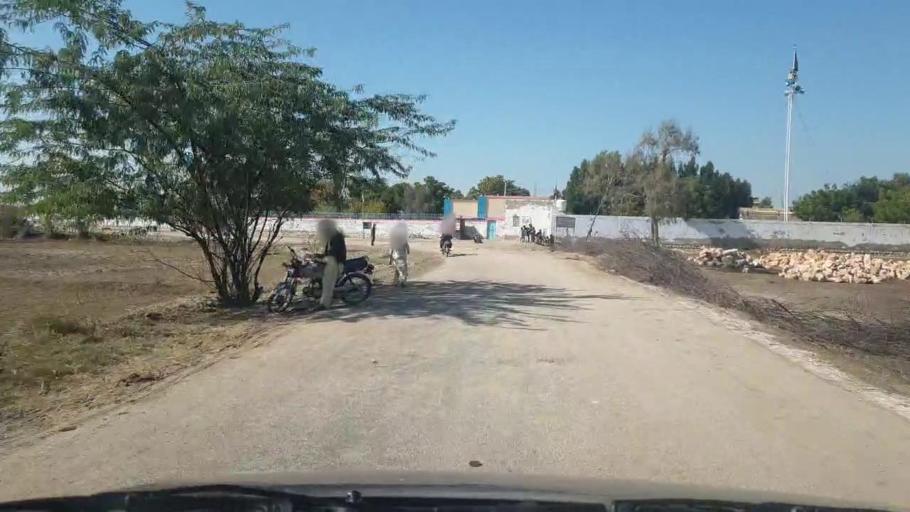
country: PK
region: Sindh
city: Bozdar
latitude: 27.1288
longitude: 68.6351
